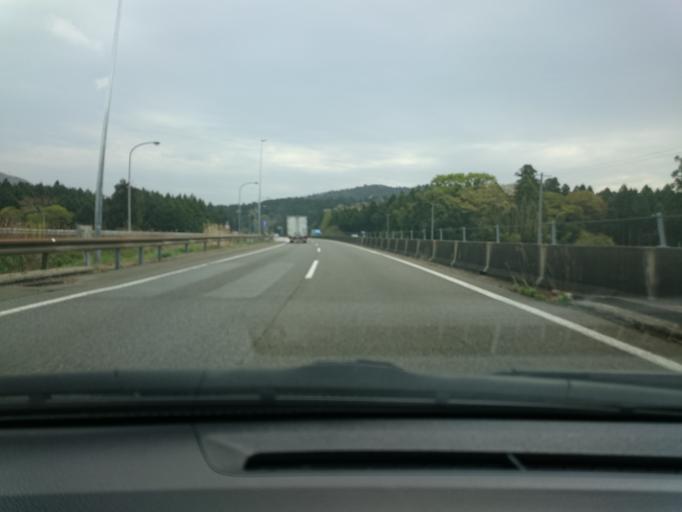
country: JP
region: Gifu
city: Tarui
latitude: 35.3331
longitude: 136.3976
